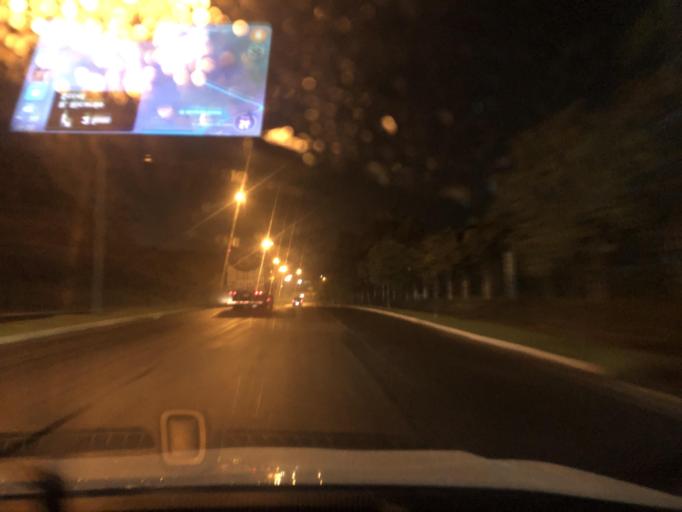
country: BR
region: Santa Catarina
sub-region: Joinville
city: Joinville
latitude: -26.3809
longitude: -48.8443
